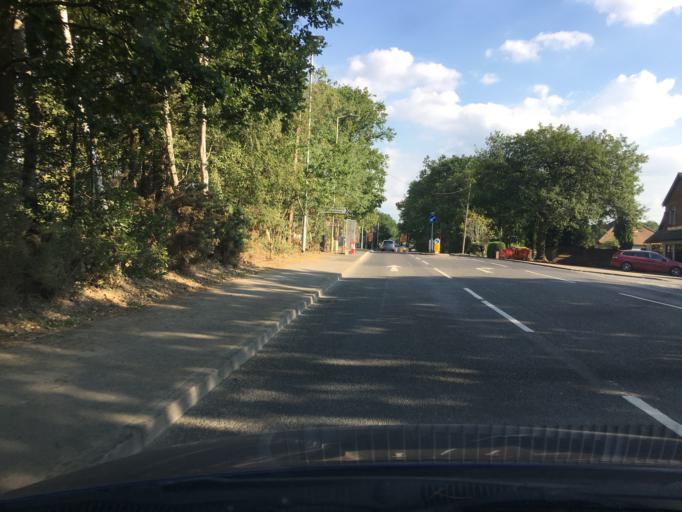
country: GB
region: England
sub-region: Bracknell Forest
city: Crowthorne
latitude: 51.3796
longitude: -0.7913
